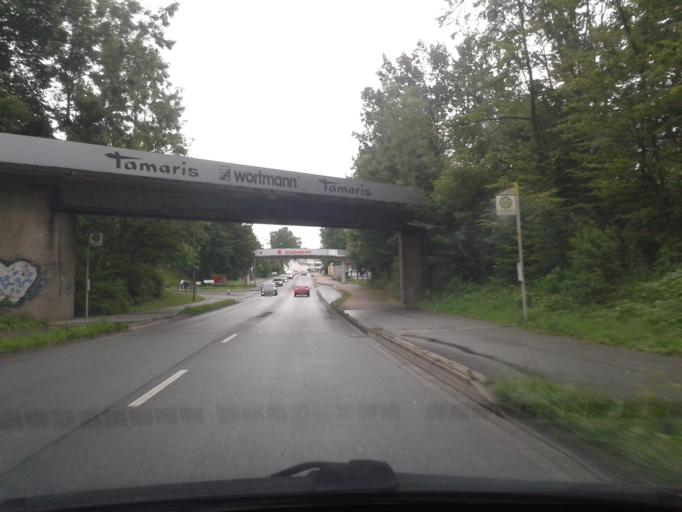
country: DE
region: North Rhine-Westphalia
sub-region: Regierungsbezirk Detmold
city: Detmold
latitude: 51.9252
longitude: 8.8952
